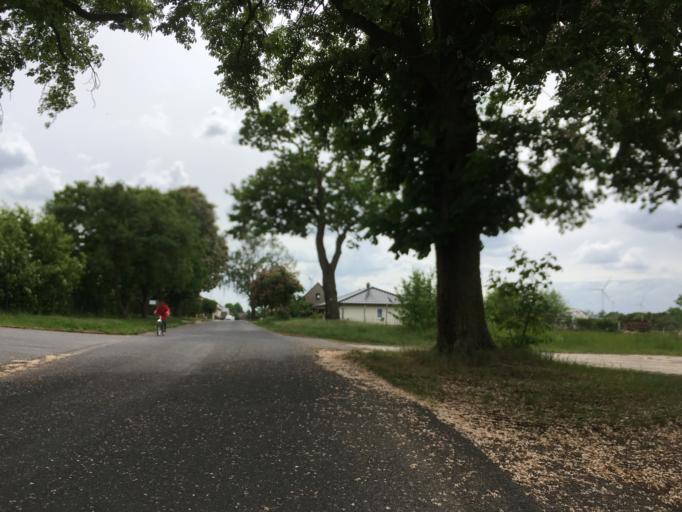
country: DE
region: Brandenburg
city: Melchow
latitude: 52.7127
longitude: 13.7236
